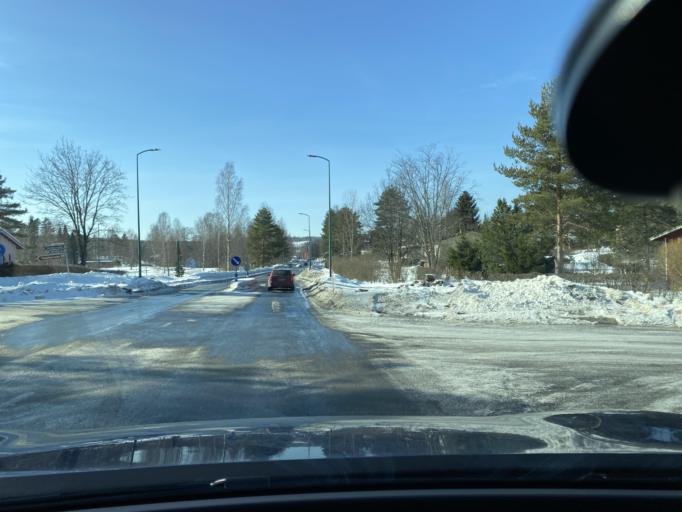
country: FI
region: Central Finland
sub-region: Jyvaeskylae
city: Korpilahti
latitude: 62.0179
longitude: 25.5688
